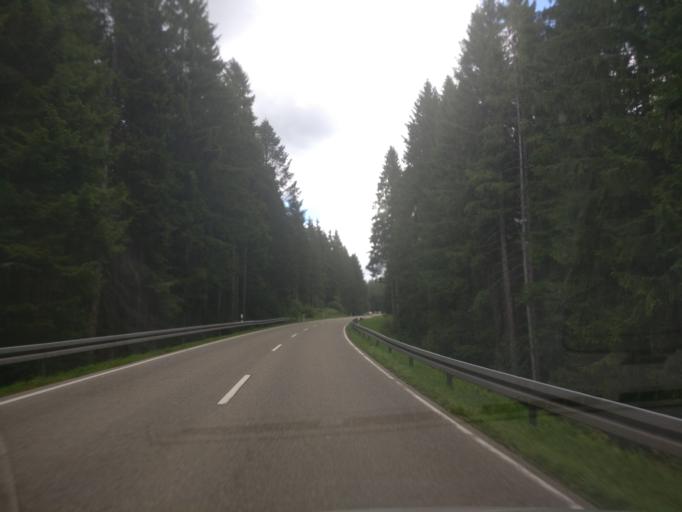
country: DE
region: Baden-Wuerttemberg
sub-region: Karlsruhe Region
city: Baiersbronn
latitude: 48.5525
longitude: 8.4259
